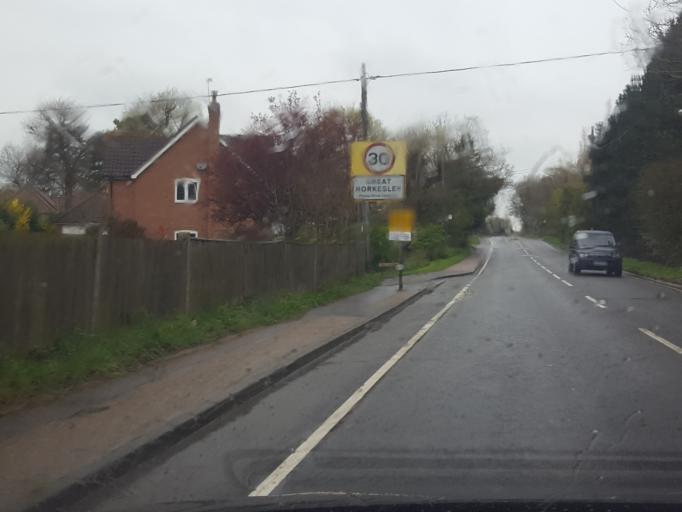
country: GB
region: England
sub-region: Essex
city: Great Horkesley
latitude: 51.9233
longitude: 0.8837
